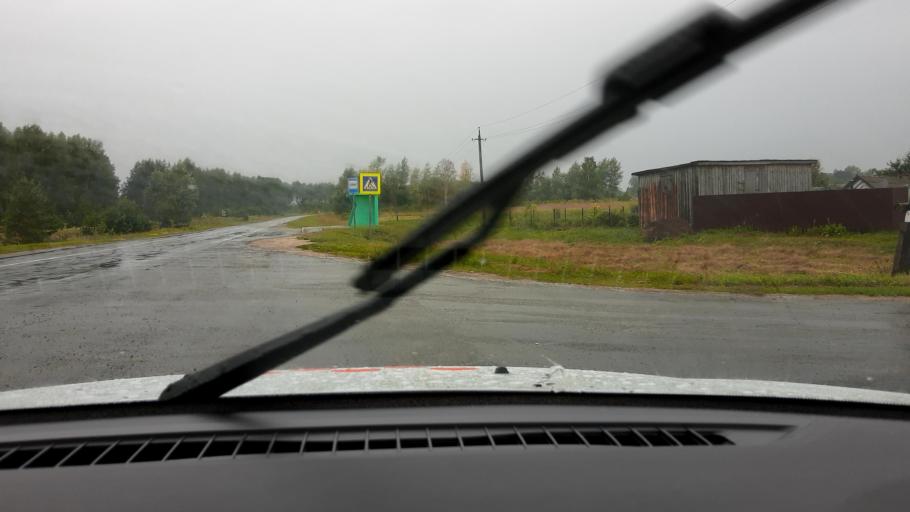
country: RU
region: Nizjnij Novgorod
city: Voznesenskoye
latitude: 54.8565
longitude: 42.8941
